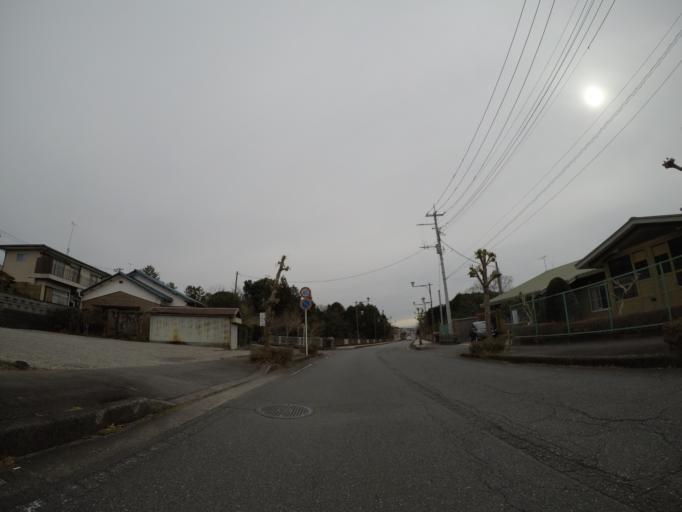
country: JP
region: Shizuoka
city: Fujinomiya
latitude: 35.2543
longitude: 138.6340
